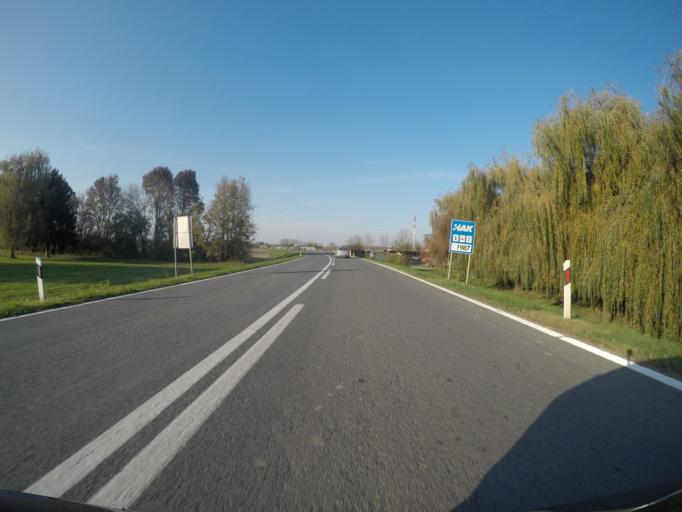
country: HU
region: Somogy
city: Barcs
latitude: 45.9352
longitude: 17.4616
